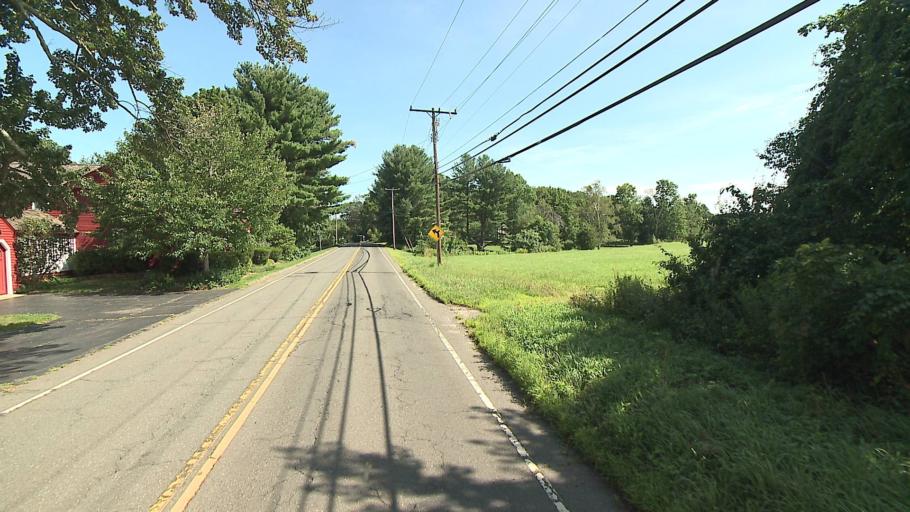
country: US
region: Connecticut
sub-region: Hartford County
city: West Simsbury
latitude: 41.8742
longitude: -72.8599
